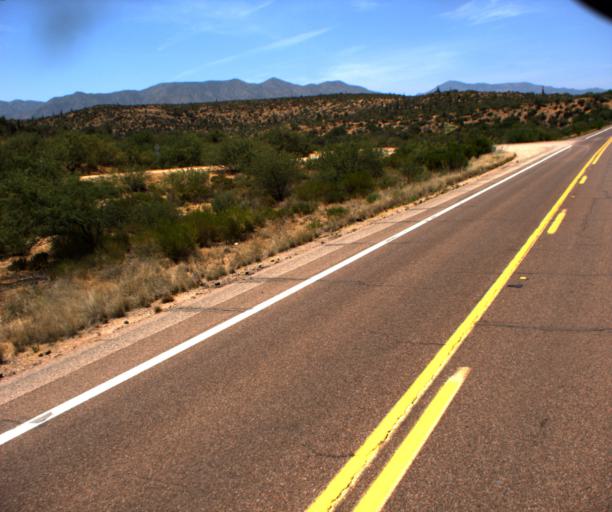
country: US
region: Arizona
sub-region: Gila County
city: Tonto Basin
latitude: 33.7878
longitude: -111.2648
